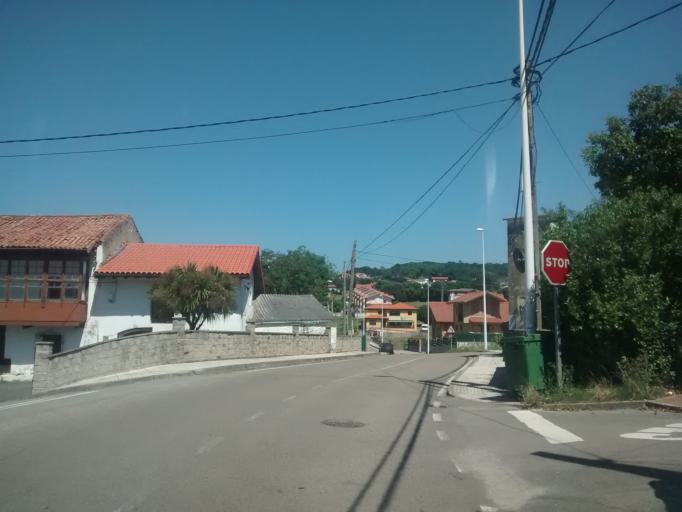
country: ES
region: Cantabria
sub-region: Provincia de Cantabria
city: Arnuero
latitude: 43.4709
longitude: -3.5680
